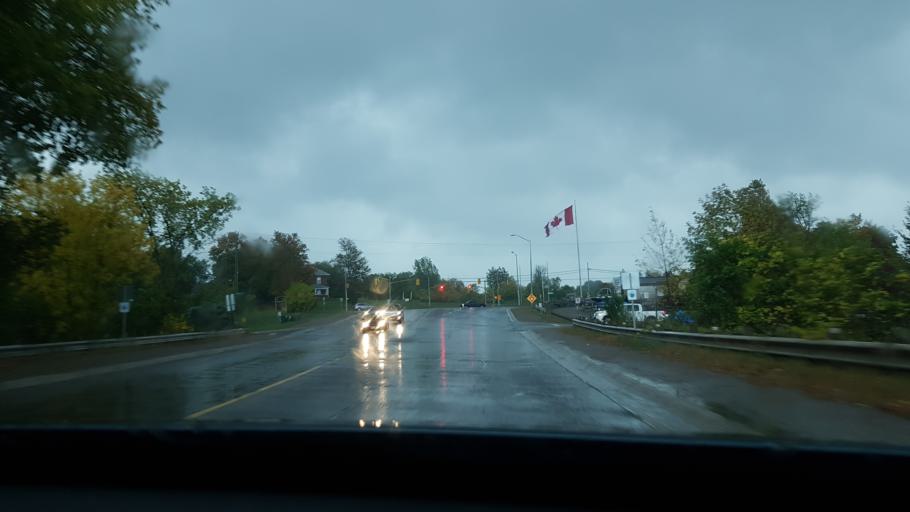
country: CA
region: Ontario
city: Peterborough
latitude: 44.3854
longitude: -78.3852
